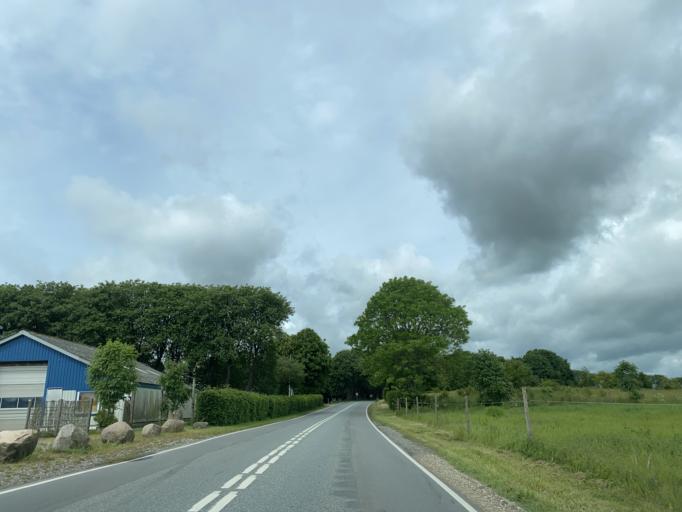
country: DK
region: Central Jutland
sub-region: Arhus Kommune
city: Stavtrup
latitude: 56.1903
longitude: 10.1404
